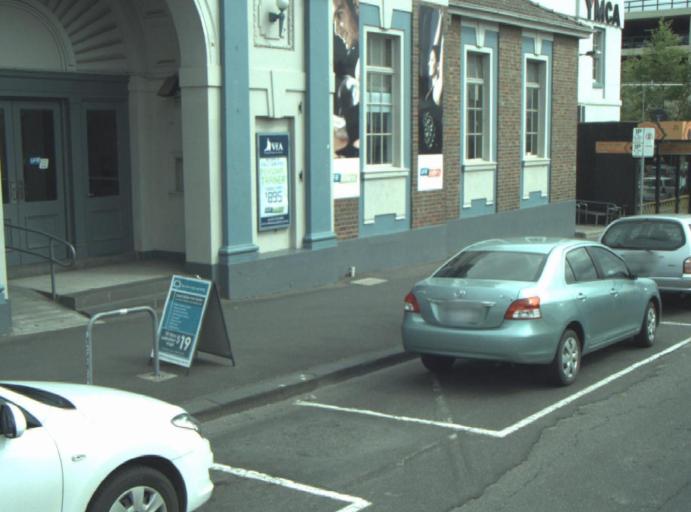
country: AU
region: Victoria
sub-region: Greater Geelong
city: Geelong
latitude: -38.1494
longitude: 144.3625
